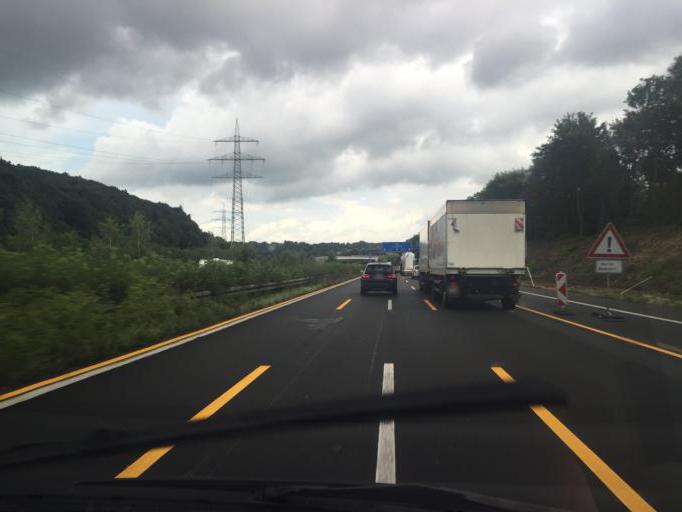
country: DE
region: North Rhine-Westphalia
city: Lohmar
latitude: 50.8464
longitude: 7.2101
